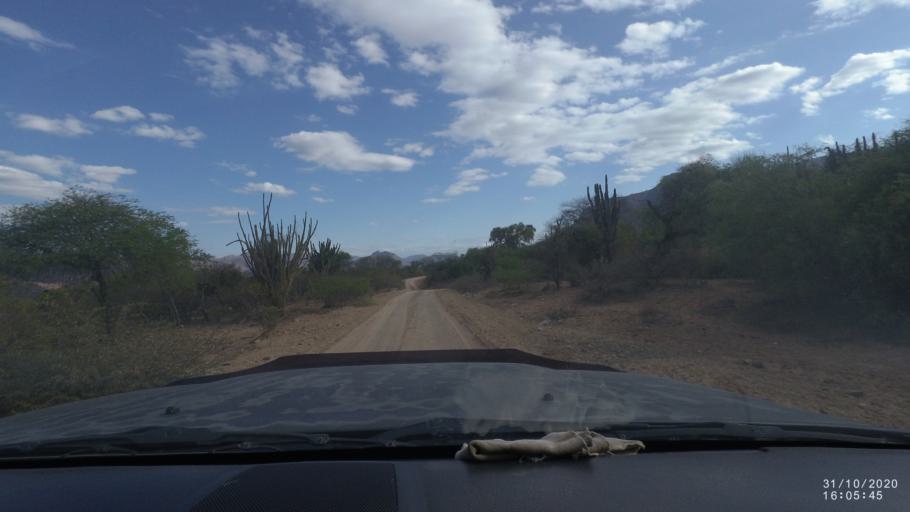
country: BO
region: Chuquisaca
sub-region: Provincia Zudanez
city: Mojocoya
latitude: -18.3688
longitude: -64.6490
